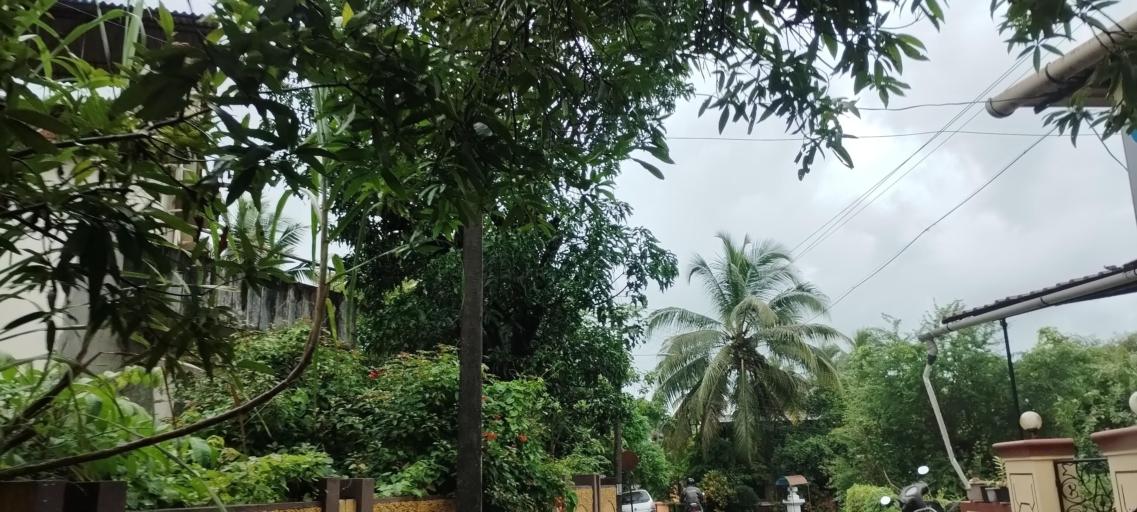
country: IN
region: Goa
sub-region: North Goa
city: Aldona
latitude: 15.5882
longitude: 73.8688
